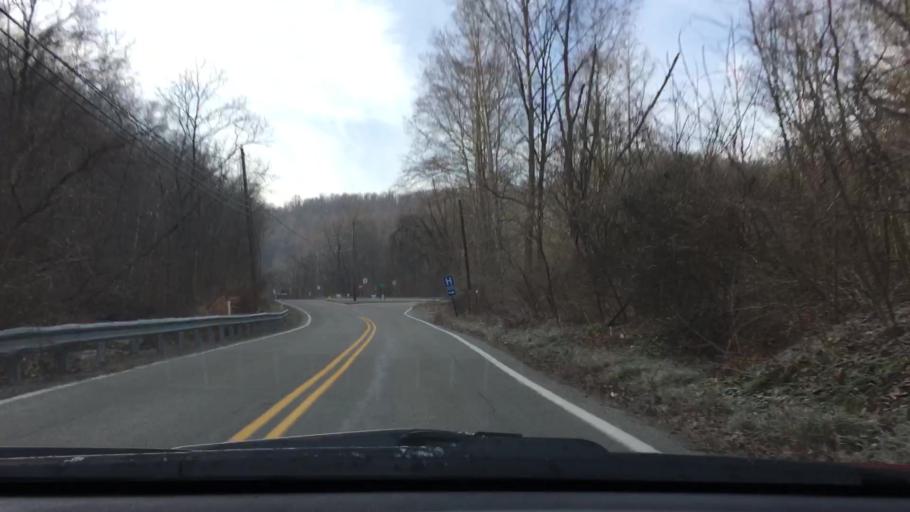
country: US
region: Pennsylvania
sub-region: Allegheny County
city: Industry
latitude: 40.2394
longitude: -79.8163
